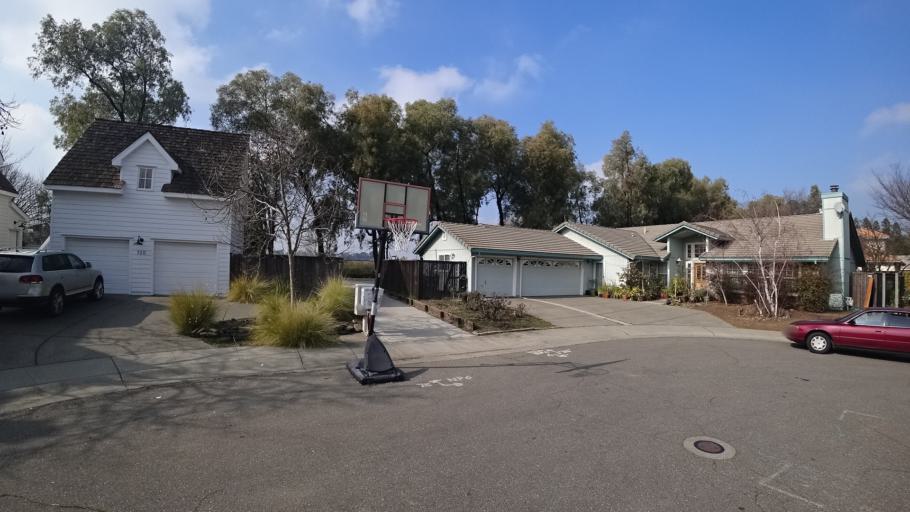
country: US
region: California
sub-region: Yolo County
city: Davis
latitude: 38.5732
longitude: -121.7575
